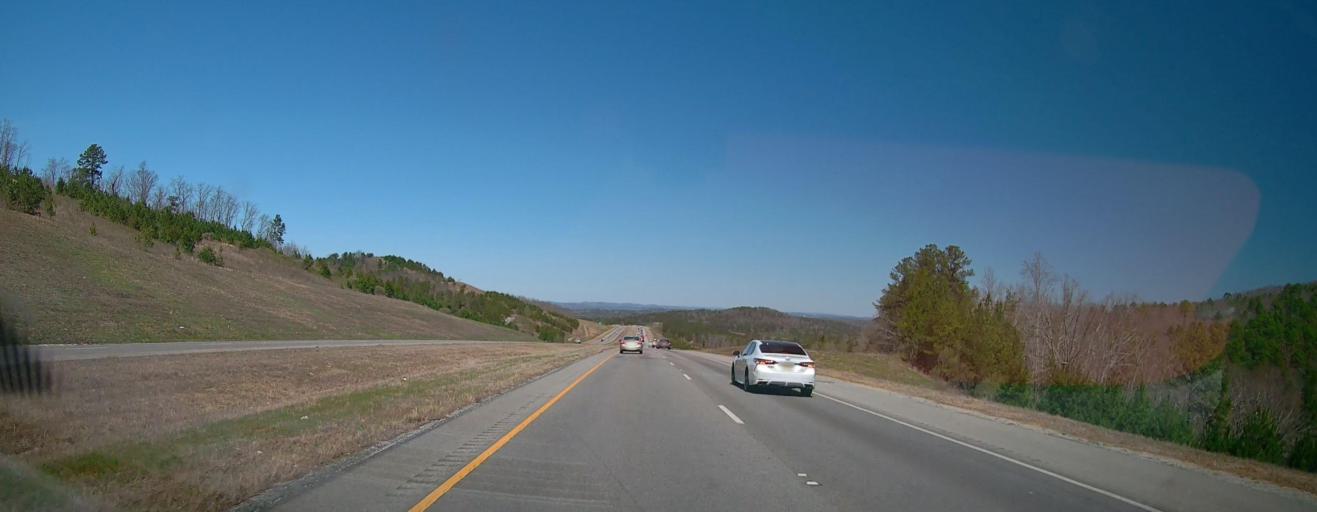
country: US
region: Alabama
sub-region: Calhoun County
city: Saks
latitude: 33.6874
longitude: -85.8043
